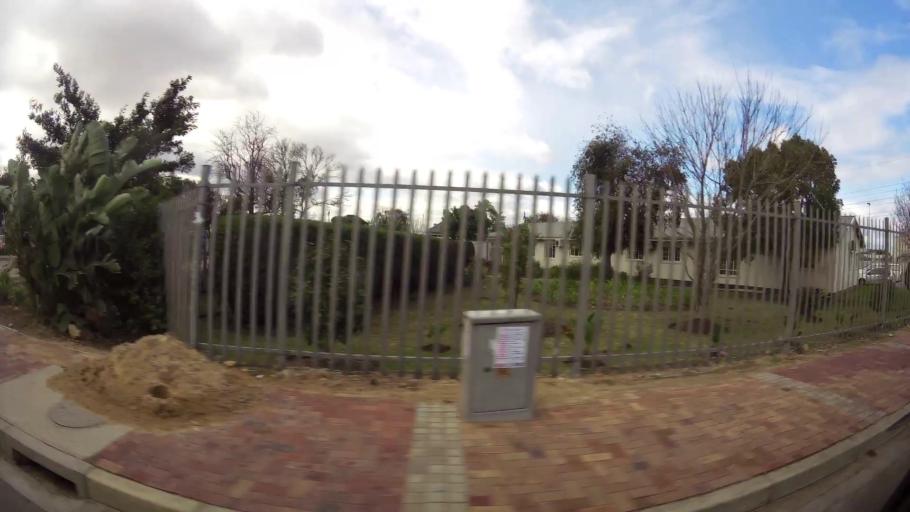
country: ZA
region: Western Cape
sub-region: Eden District Municipality
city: George
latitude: -33.9803
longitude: 22.4719
